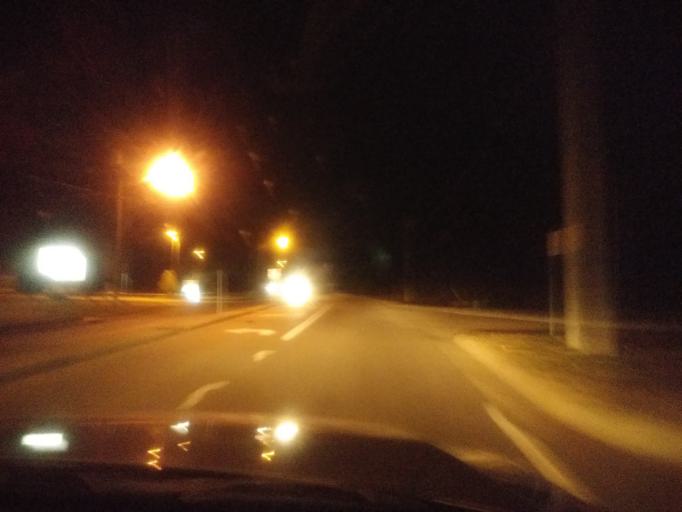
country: US
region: Virginia
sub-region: City of Chesapeake
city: Chesapeake
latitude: 36.7884
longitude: -76.1960
